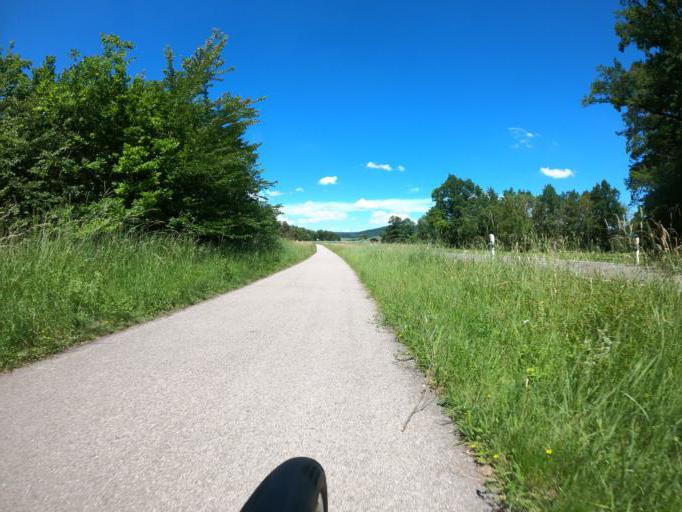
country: DE
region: Baden-Wuerttemberg
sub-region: Regierungsbezirk Stuttgart
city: Sersheim
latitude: 48.9816
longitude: 9.0230
